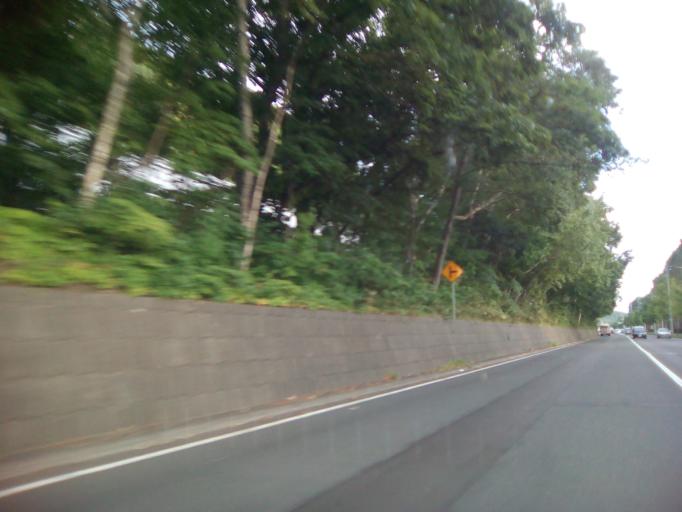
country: JP
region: Hokkaido
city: Sapporo
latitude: 42.9949
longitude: 141.3588
